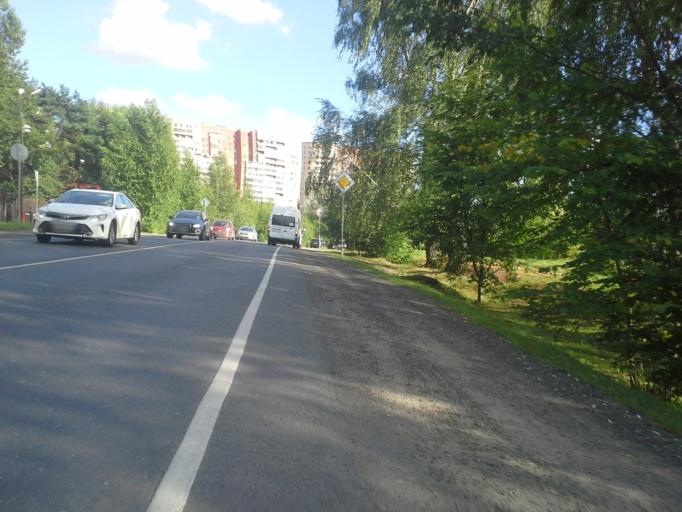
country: RU
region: Moskovskaya
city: Troitsk
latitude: 55.4959
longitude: 37.2953
